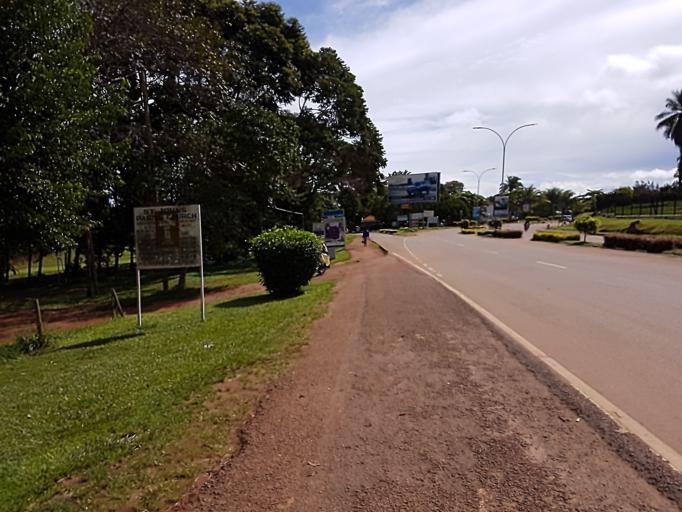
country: UG
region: Central Region
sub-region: Wakiso District
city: Entebbe
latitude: 0.0562
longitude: 32.4695
